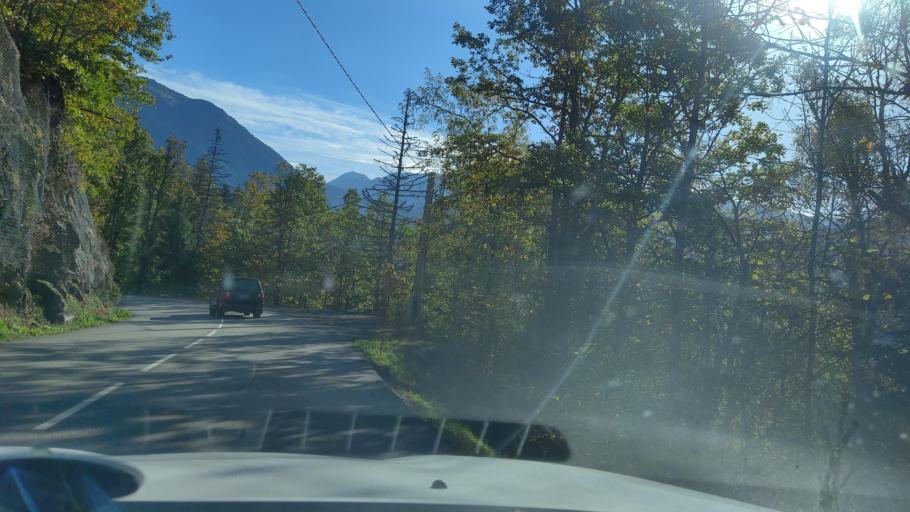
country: FR
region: Rhone-Alpes
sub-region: Departement de la Savoie
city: Beaufort
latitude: 45.7314
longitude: 6.5424
